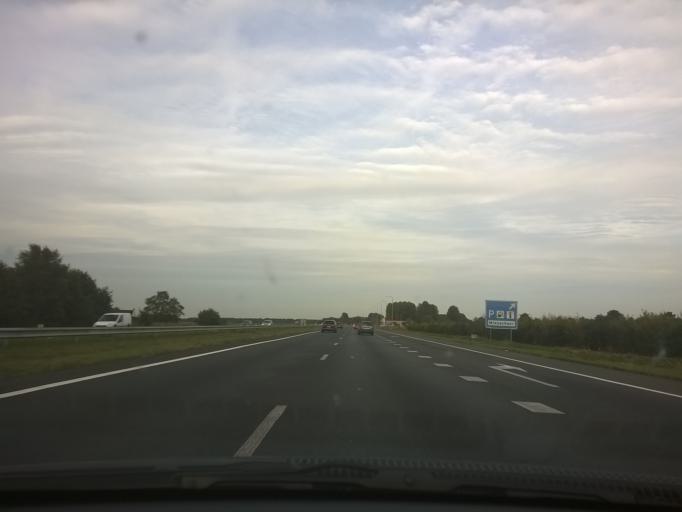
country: NL
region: Groningen
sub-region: Gemeente Grootegast
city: Grootegast
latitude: 53.1595
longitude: 6.2863
